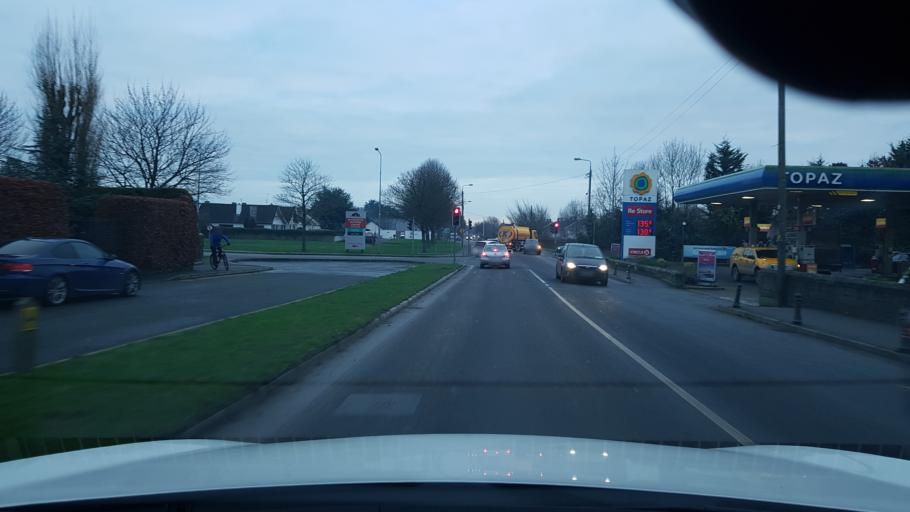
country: IE
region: Leinster
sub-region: An Mhi
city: Navan
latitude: 53.6636
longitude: -6.6801
